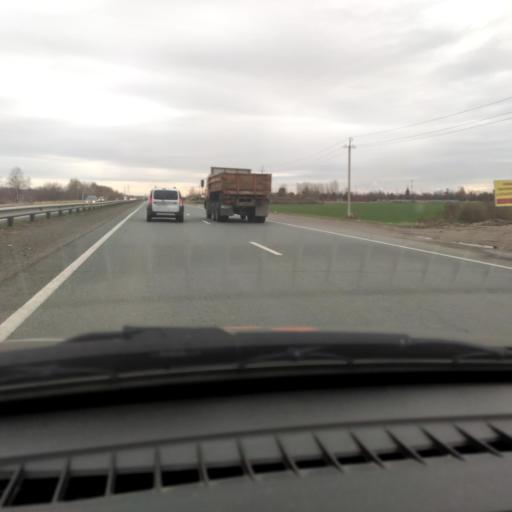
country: RU
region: Samara
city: Tol'yatti
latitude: 53.5779
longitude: 49.4171
